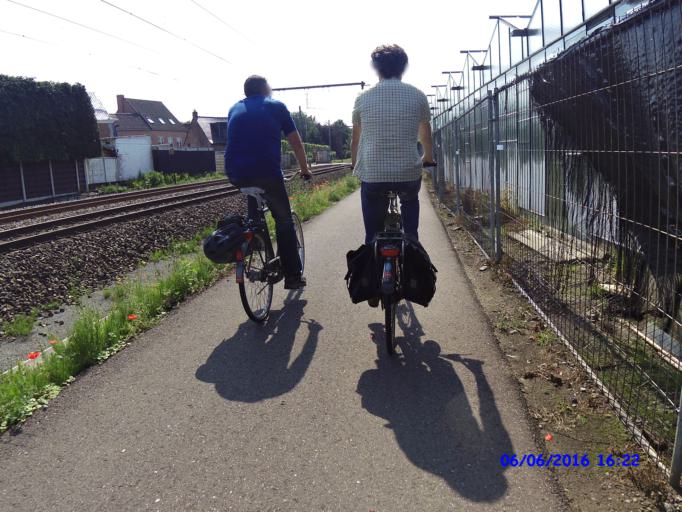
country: BE
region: Flanders
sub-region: Provincie Oost-Vlaanderen
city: Lokeren
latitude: 51.0999
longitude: 3.9526
